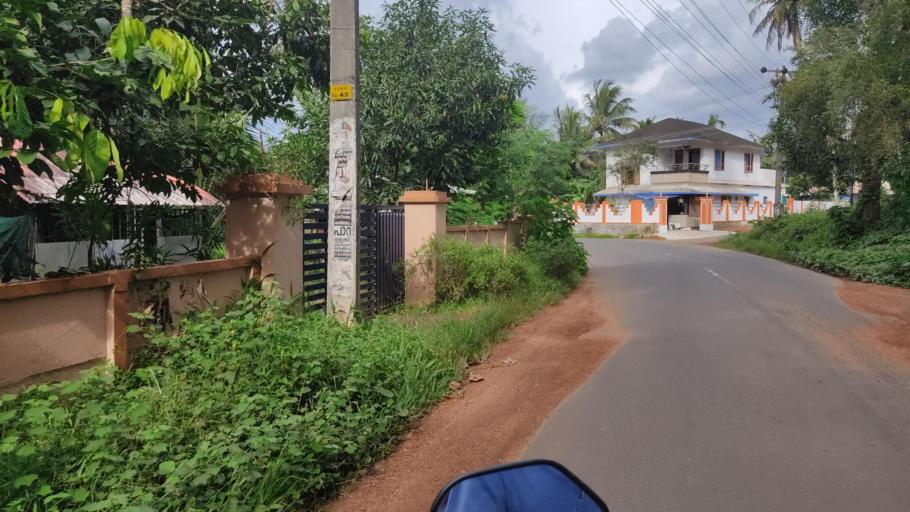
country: IN
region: Kerala
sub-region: Pattanamtitta
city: Adur
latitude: 9.1942
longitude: 76.7774
